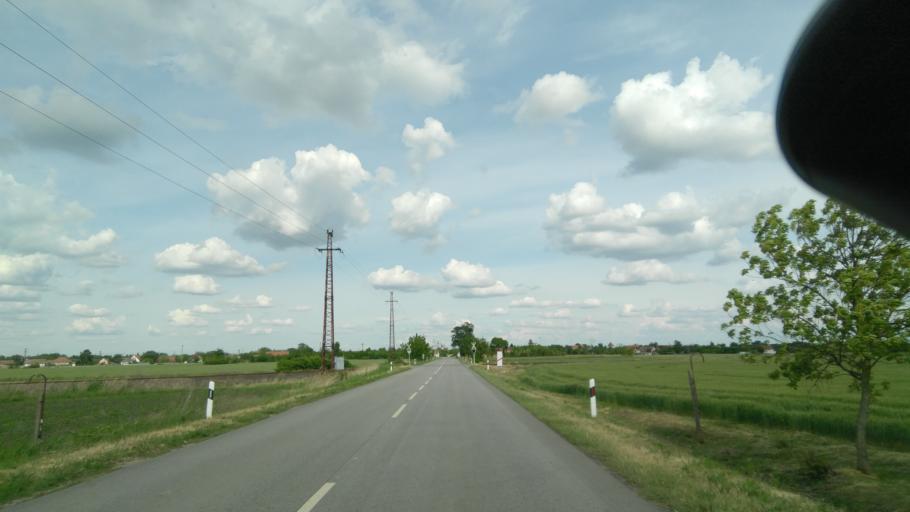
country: HU
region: Bekes
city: Battonya
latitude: 46.2917
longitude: 20.9954
